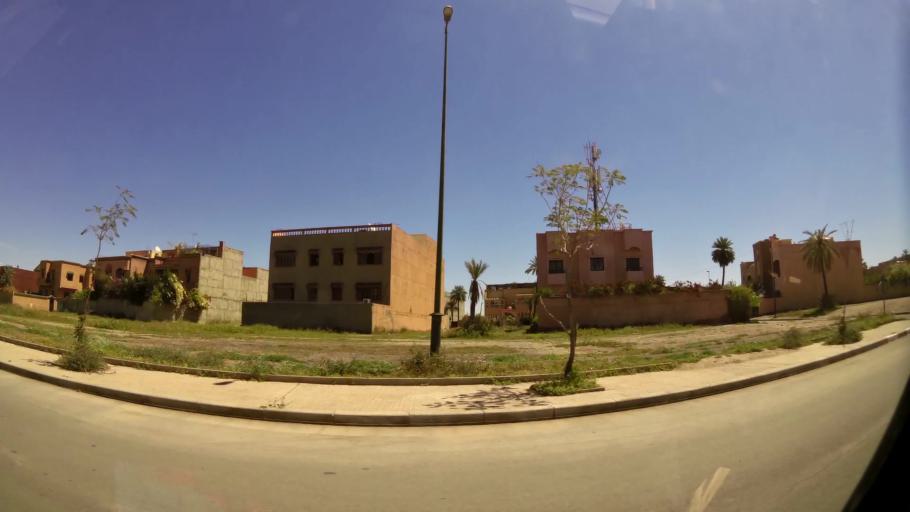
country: MA
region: Marrakech-Tensift-Al Haouz
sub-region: Marrakech
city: Marrakesh
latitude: 31.6488
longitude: -7.9892
